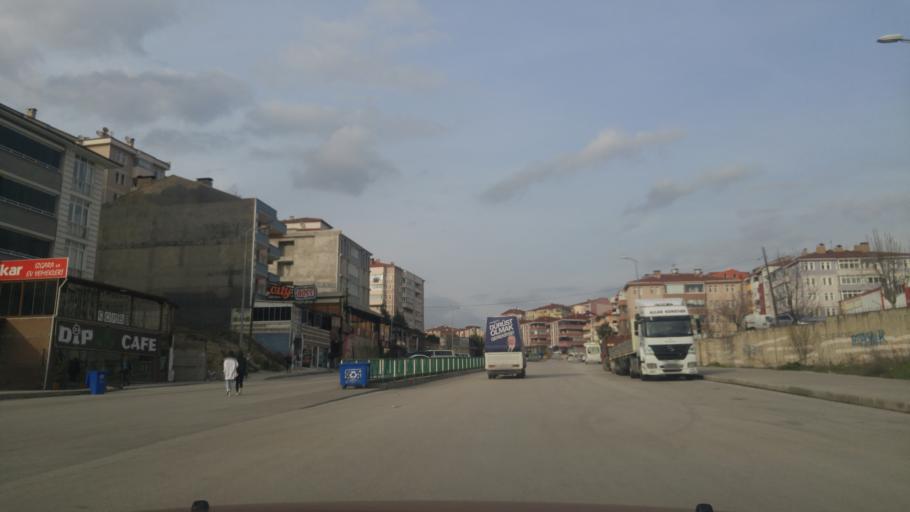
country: TR
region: Karabuk
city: Karabuk
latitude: 41.2208
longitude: 32.6608
